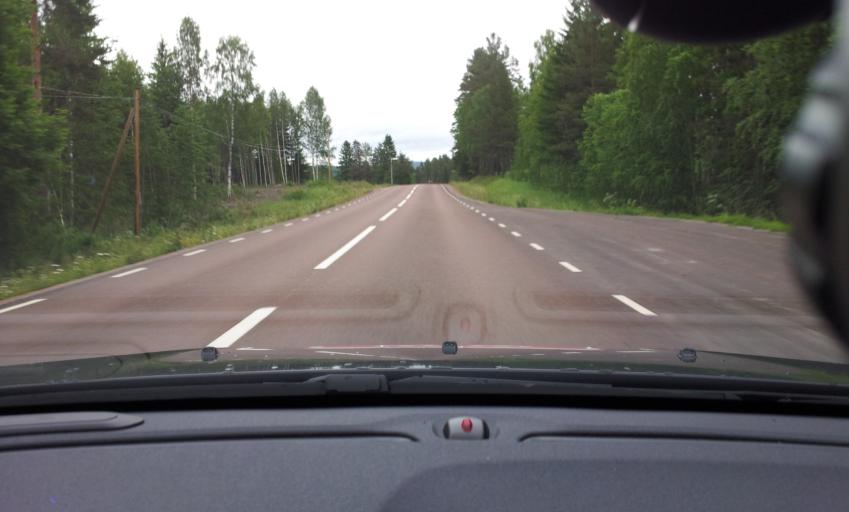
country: SE
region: Jaemtland
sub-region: Ragunda Kommun
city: Hammarstrand
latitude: 63.0187
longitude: 16.5761
